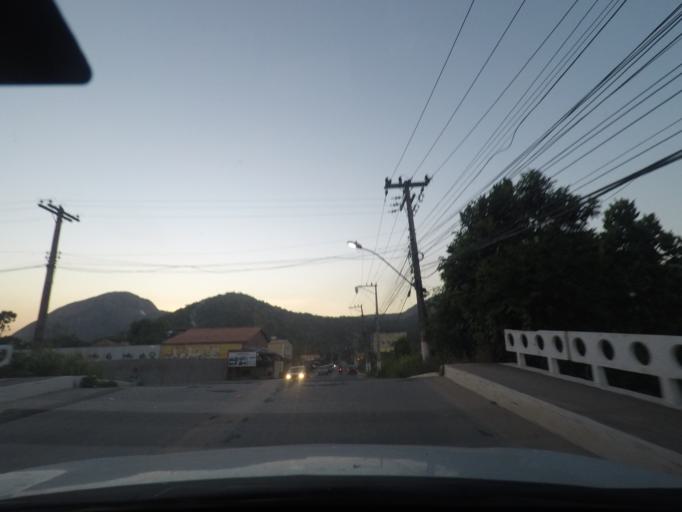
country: BR
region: Rio de Janeiro
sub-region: Niteroi
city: Niteroi
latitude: -22.9621
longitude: -43.0005
